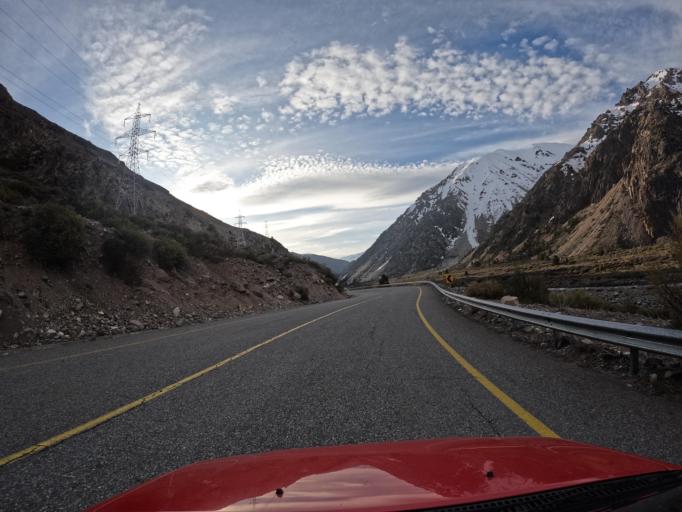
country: CL
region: Maule
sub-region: Provincia de Linares
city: Colbun
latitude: -35.8863
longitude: -70.6550
